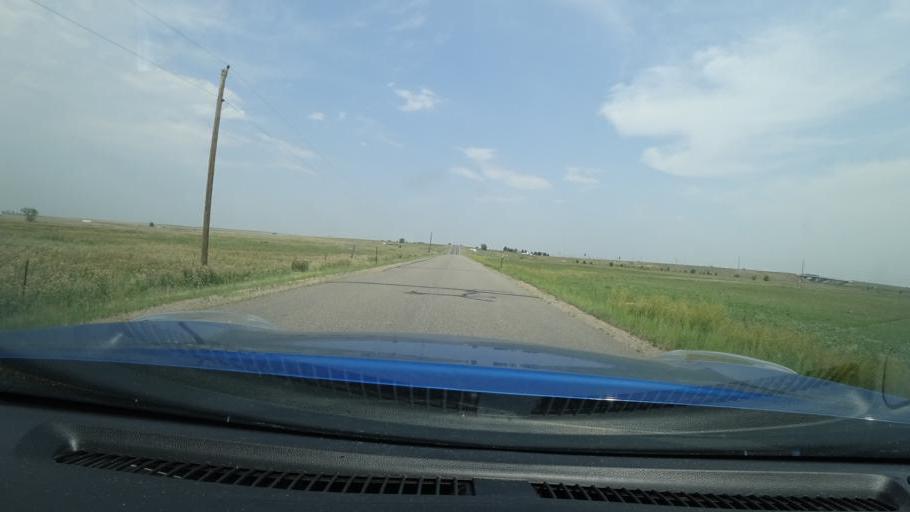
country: US
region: Colorado
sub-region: Adams County
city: Aurora
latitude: 39.7547
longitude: -104.7235
